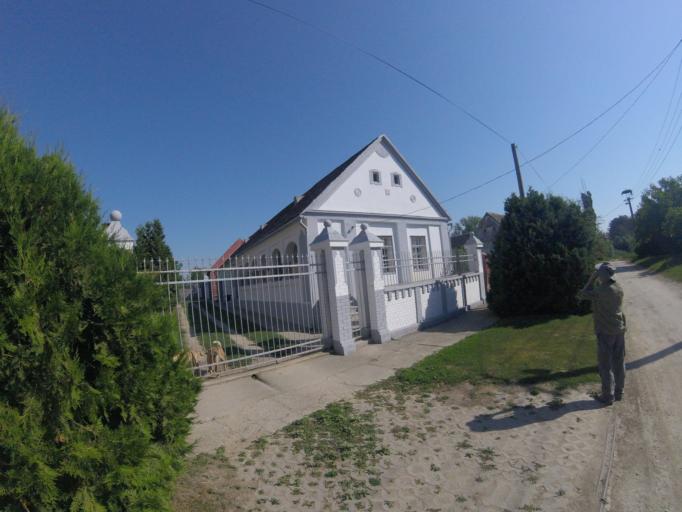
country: HU
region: Baranya
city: Sellye
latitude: 45.9287
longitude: 17.8802
